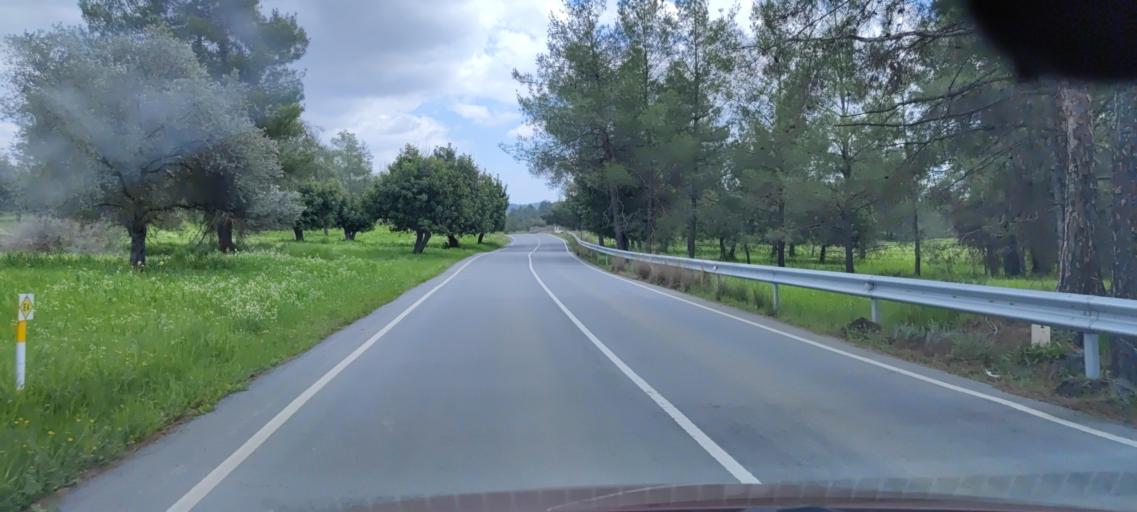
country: CY
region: Larnaka
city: Kornos
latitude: 34.9192
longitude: 33.3535
